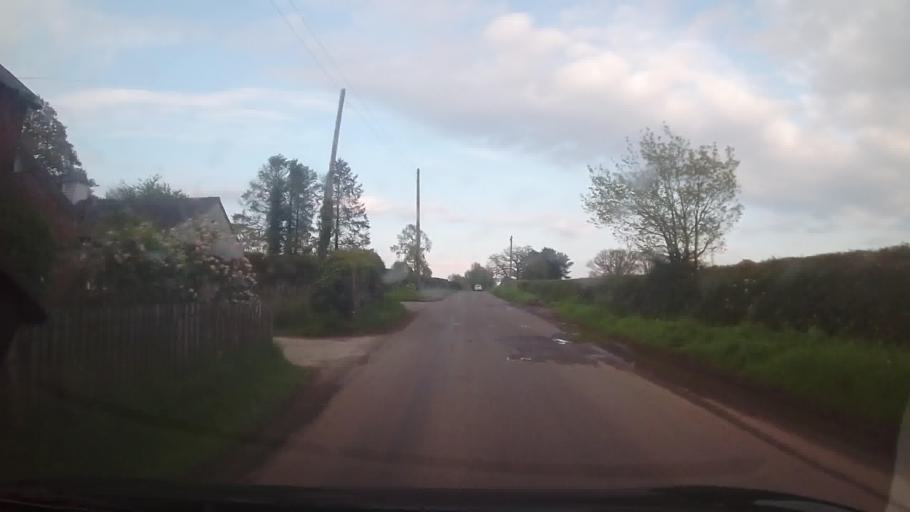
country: GB
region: England
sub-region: Shropshire
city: Ellesmere
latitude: 52.9368
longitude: -2.8892
